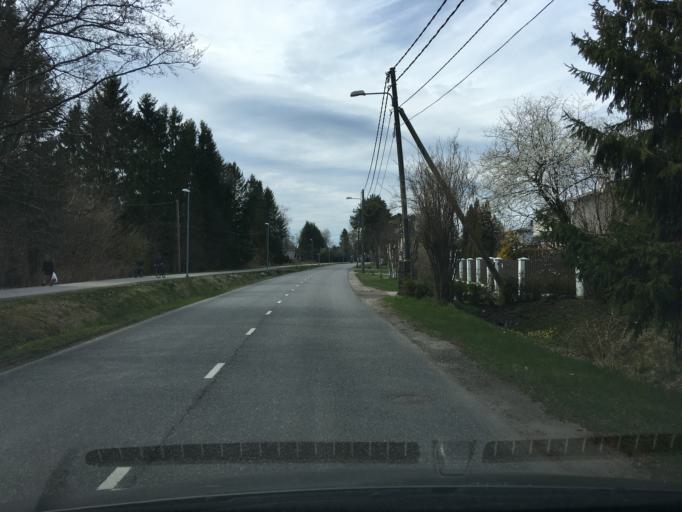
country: EE
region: Harju
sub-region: Joelaehtme vald
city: Loo
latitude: 59.4733
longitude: 24.9349
